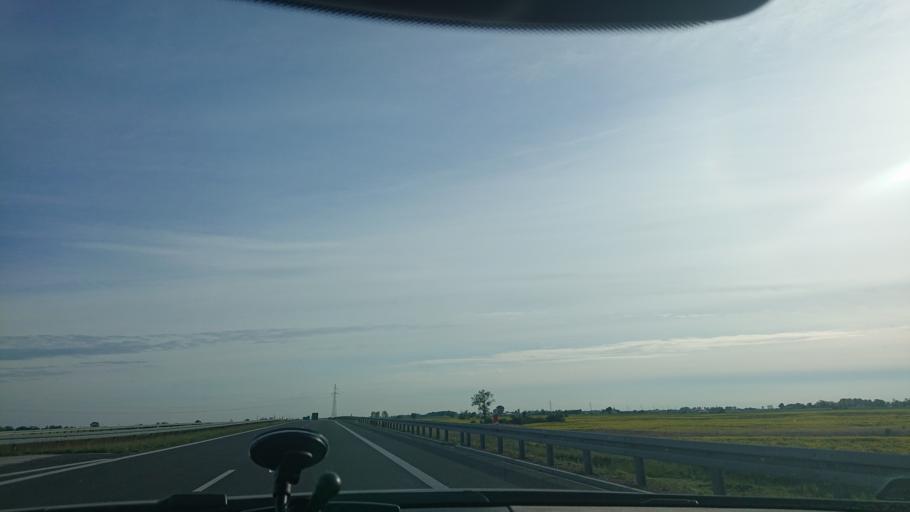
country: PL
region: Greater Poland Voivodeship
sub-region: Powiat gnieznienski
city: Gniezno
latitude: 52.5344
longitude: 17.5188
